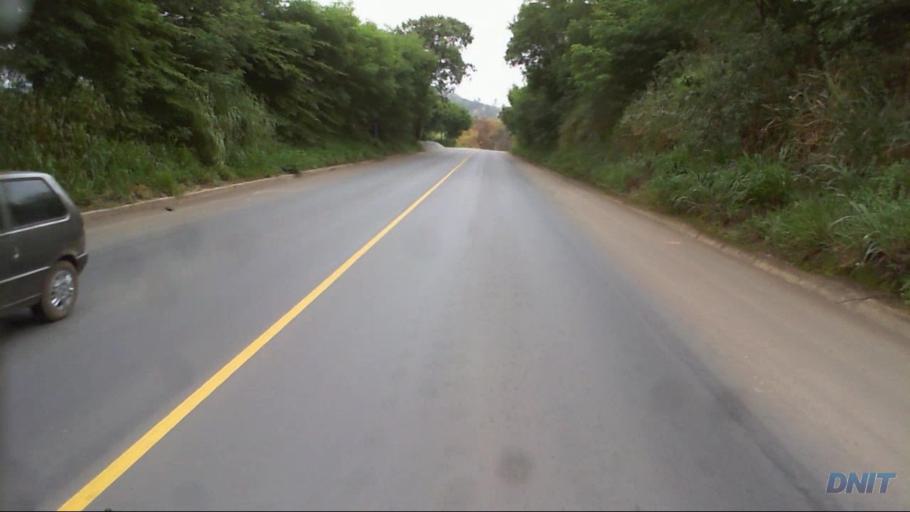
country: BR
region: Minas Gerais
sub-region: Coronel Fabriciano
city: Coronel Fabriciano
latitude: -19.5248
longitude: -42.6603
